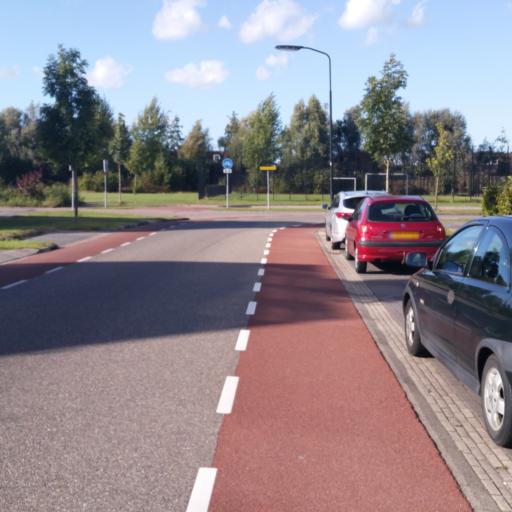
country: NL
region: Utrecht
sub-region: Gemeente IJsselstein
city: IJsselstein
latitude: 52.0075
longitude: 5.0361
